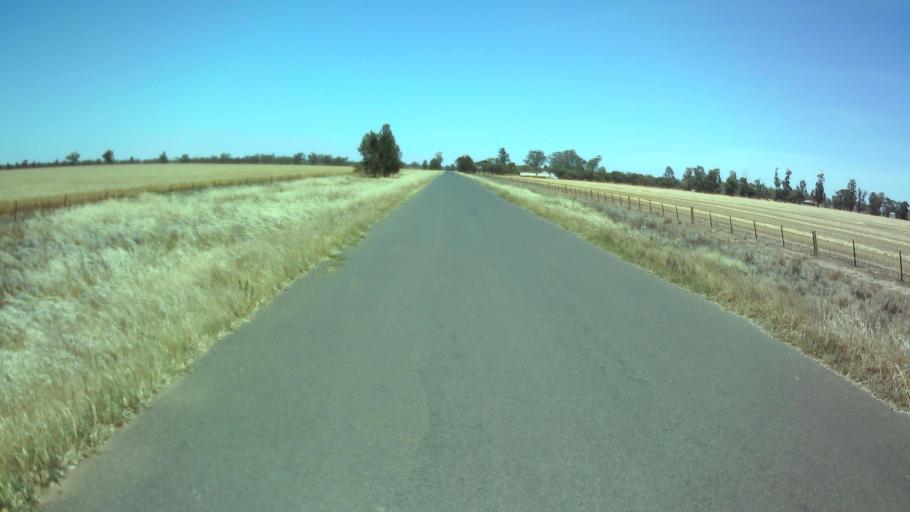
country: AU
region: New South Wales
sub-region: Weddin
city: Grenfell
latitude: -34.0262
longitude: 147.7916
